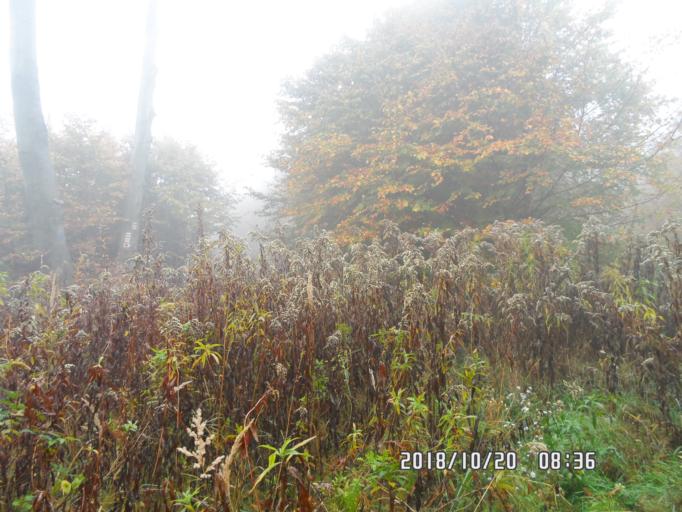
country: HU
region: Veszprem
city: Herend
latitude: 47.2004
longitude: 17.7492
